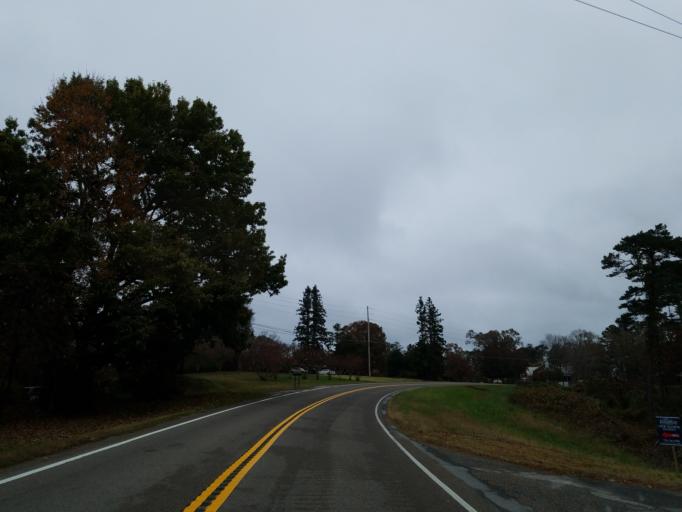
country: US
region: Georgia
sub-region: Cherokee County
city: Canton
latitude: 34.2744
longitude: -84.5806
